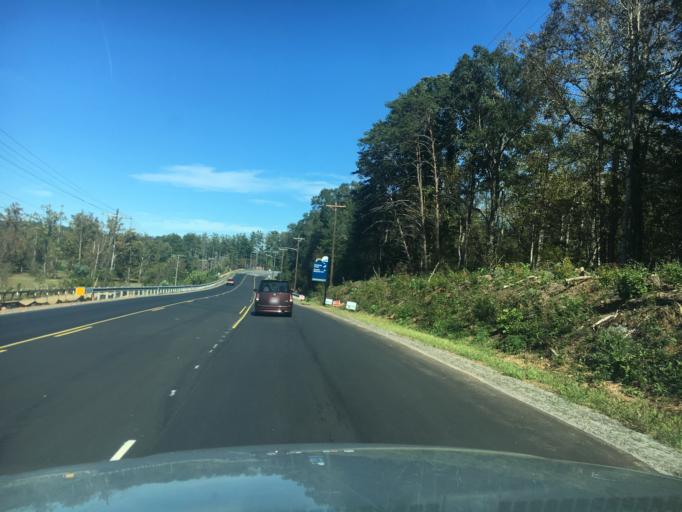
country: US
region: North Carolina
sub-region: Burke County
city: Morganton
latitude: 35.7560
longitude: -81.7028
